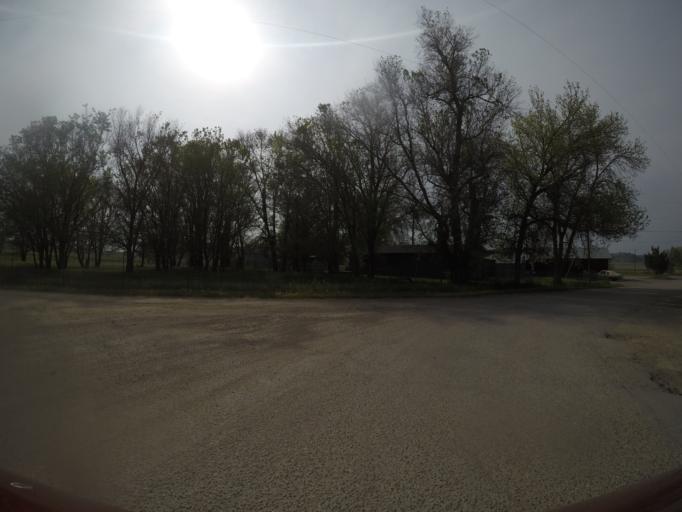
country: US
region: Montana
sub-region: Yellowstone County
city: Laurel
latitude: 45.4815
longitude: -108.9783
